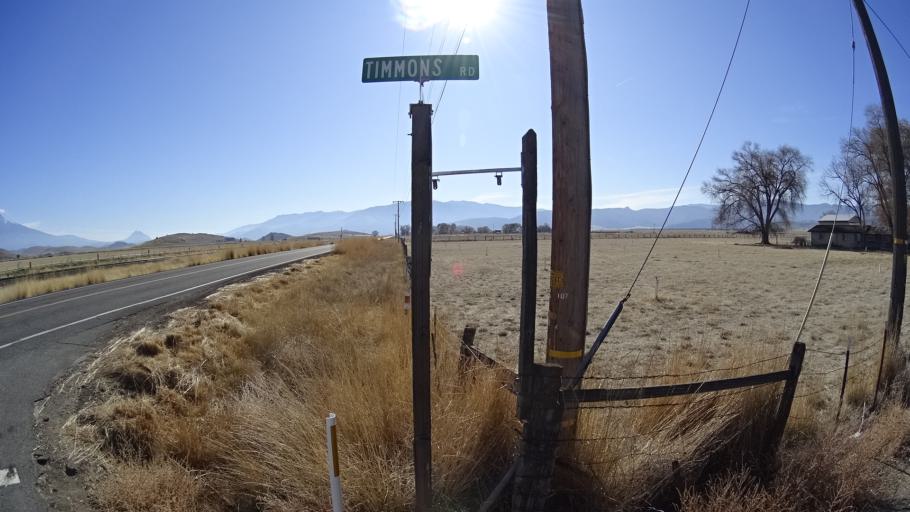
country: US
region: California
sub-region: Siskiyou County
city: Montague
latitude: 41.5746
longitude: -122.5251
